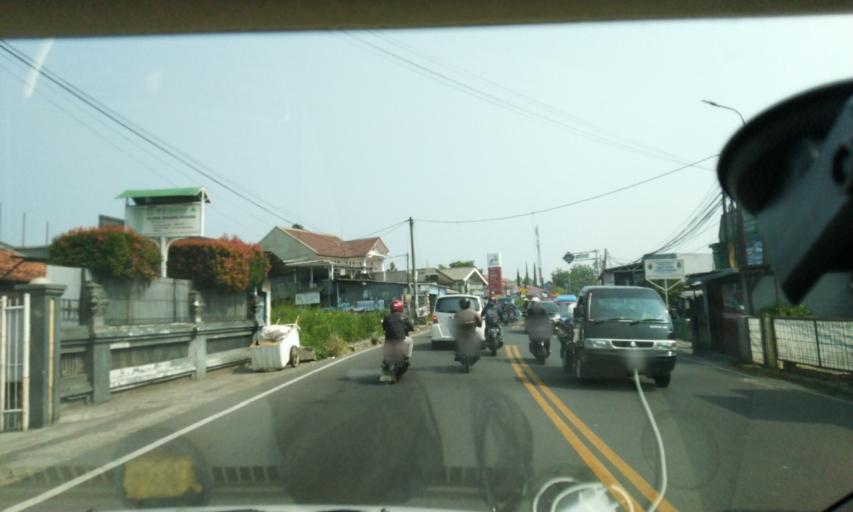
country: ID
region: West Java
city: Caringin
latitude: -6.6630
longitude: 106.8548
